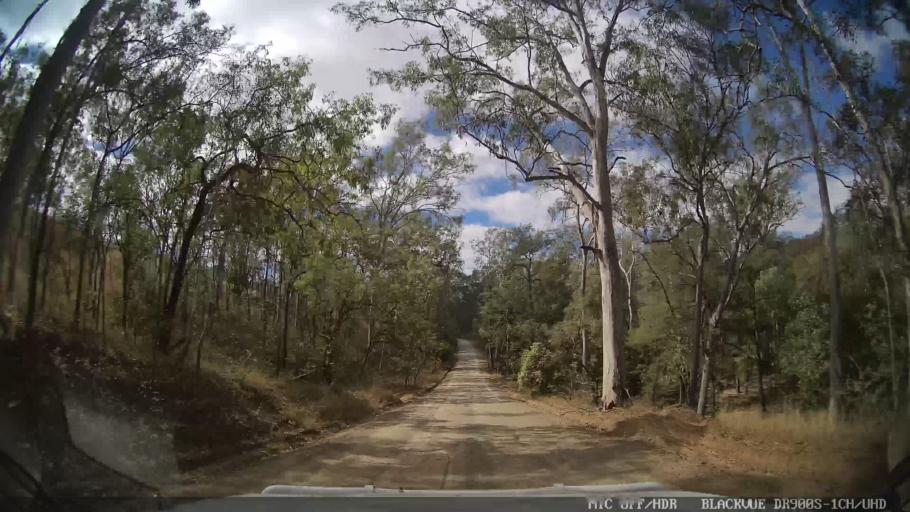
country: AU
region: Queensland
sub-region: Gladstone
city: Toolooa
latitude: -24.5515
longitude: 151.3381
